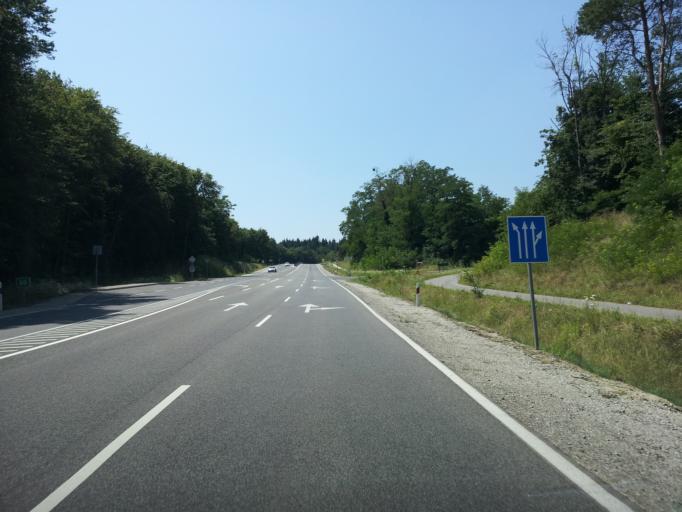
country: HU
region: Zala
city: Zalaegerszeg
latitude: 46.8443
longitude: 16.9041
